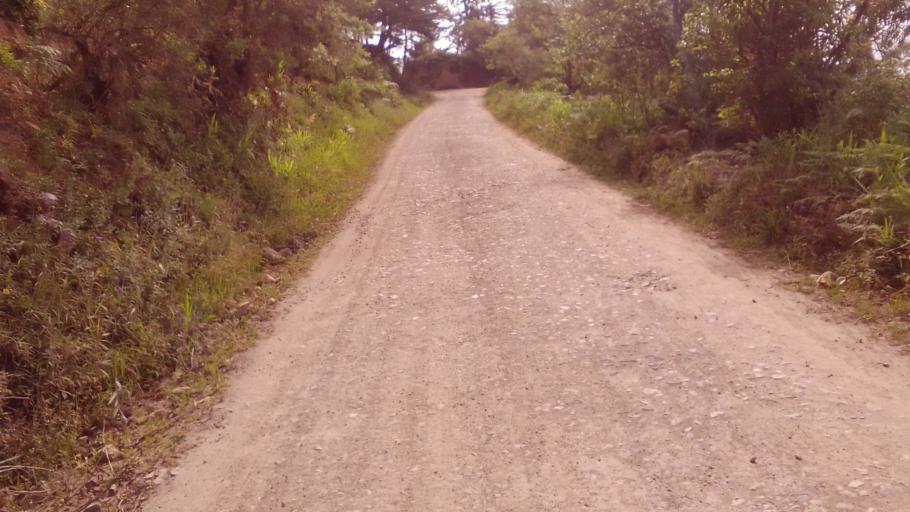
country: CO
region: Cundinamarca
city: Tenza
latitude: 5.1010
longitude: -73.4177
